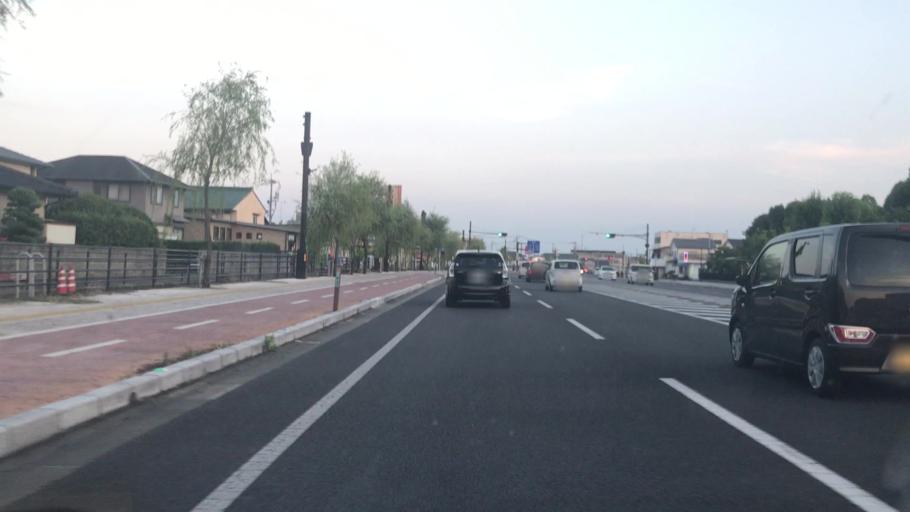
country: JP
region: Saga Prefecture
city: Saga-shi
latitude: 33.2424
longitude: 130.2941
